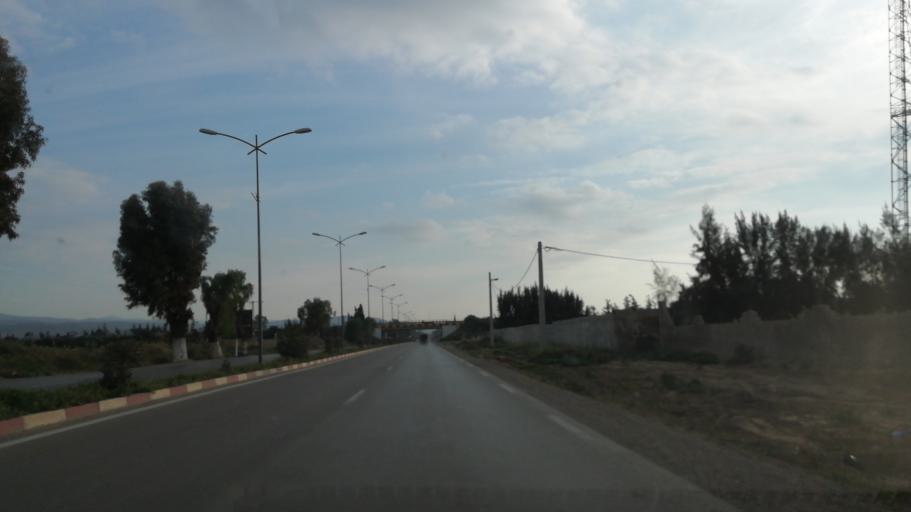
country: DZ
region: Mascara
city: Mascara
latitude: 35.6249
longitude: 0.0617
